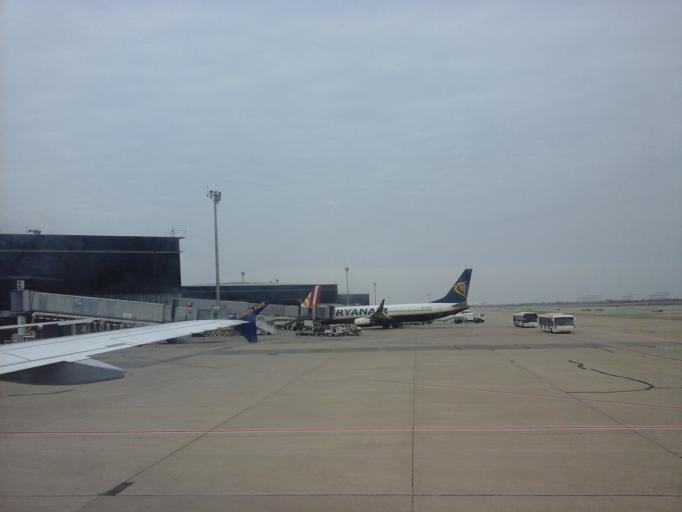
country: ES
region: Catalonia
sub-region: Provincia de Barcelona
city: El Prat de Llobregat
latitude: 41.3008
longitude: 2.0763
